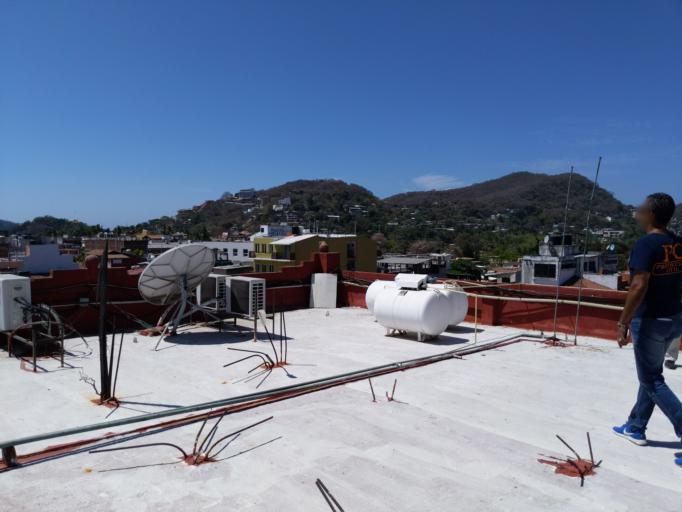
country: MX
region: Guerrero
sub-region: Zihuatanejo de Azueta
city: Ixtapa-Zihuatanejo
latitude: 17.6411
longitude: -101.5581
